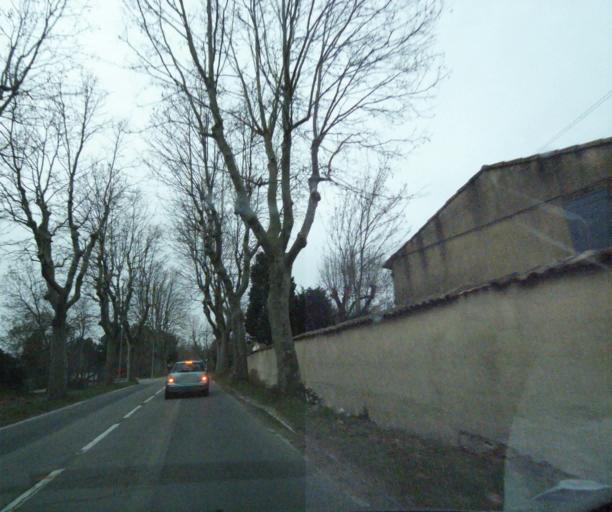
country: FR
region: Provence-Alpes-Cote d'Azur
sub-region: Departement des Bouches-du-Rhone
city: Aix-en-Provence
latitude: 43.5592
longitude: 5.4613
